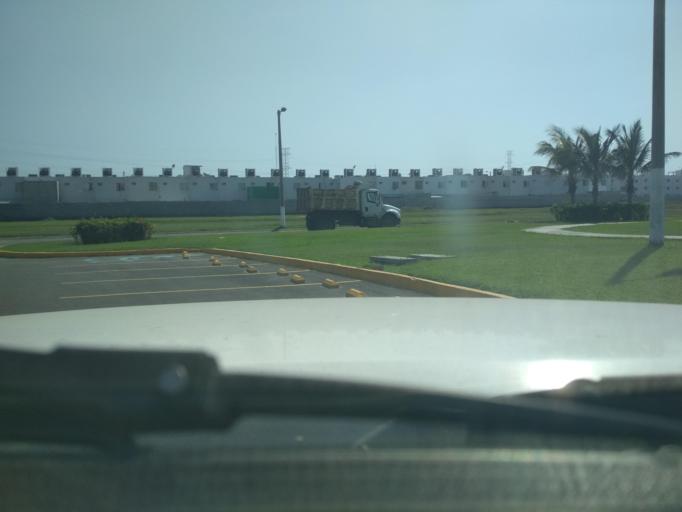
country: MX
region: Veracruz
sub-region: Veracruz
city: Las Amapolas
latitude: 19.1583
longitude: -96.2221
